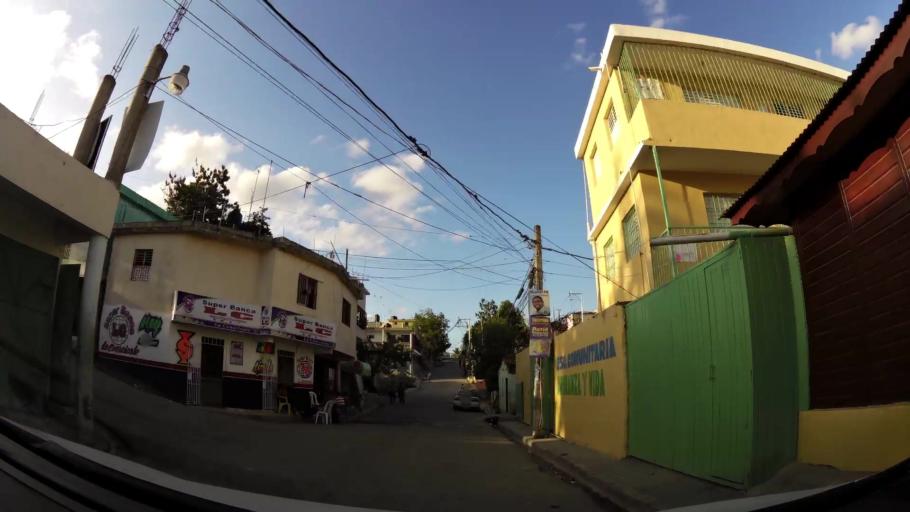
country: DO
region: Nacional
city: La Agustina
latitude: 18.5428
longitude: -69.9248
